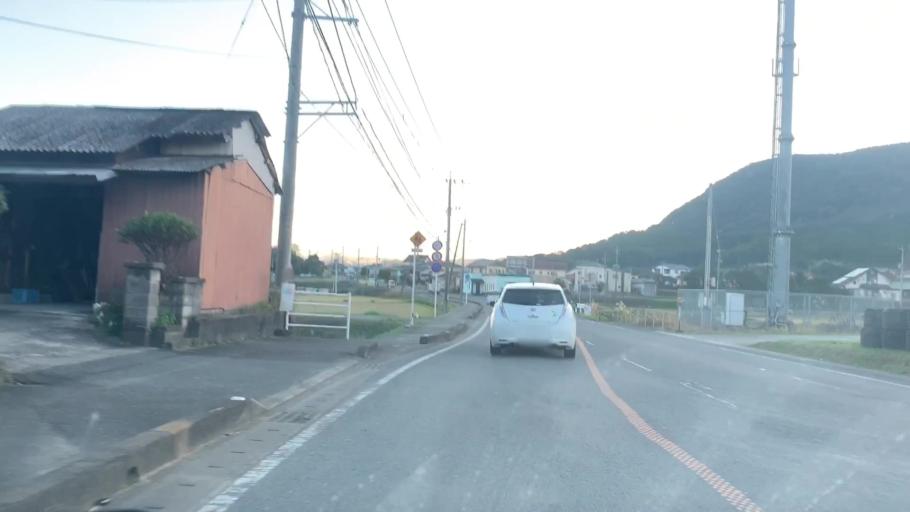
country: JP
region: Saga Prefecture
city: Takeocho-takeo
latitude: 33.2214
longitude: 130.0280
